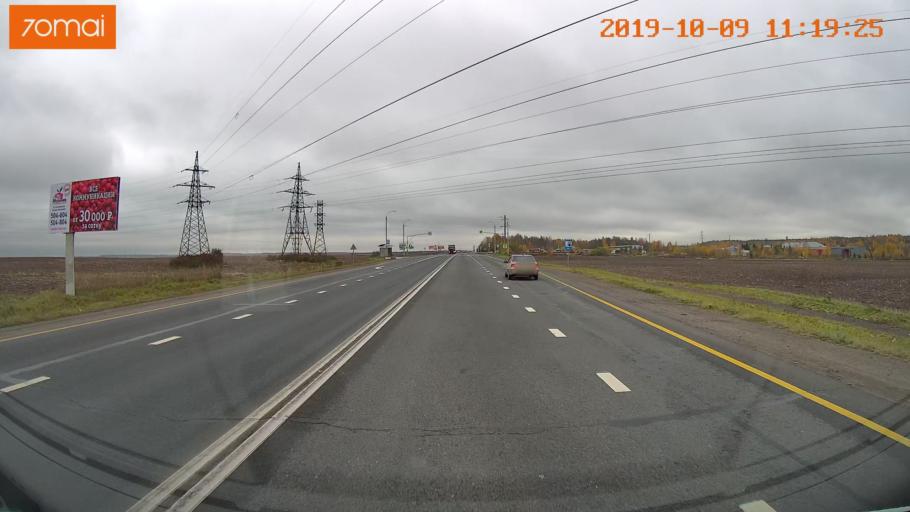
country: RU
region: Vologda
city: Vologda
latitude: 59.1621
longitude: 39.9276
